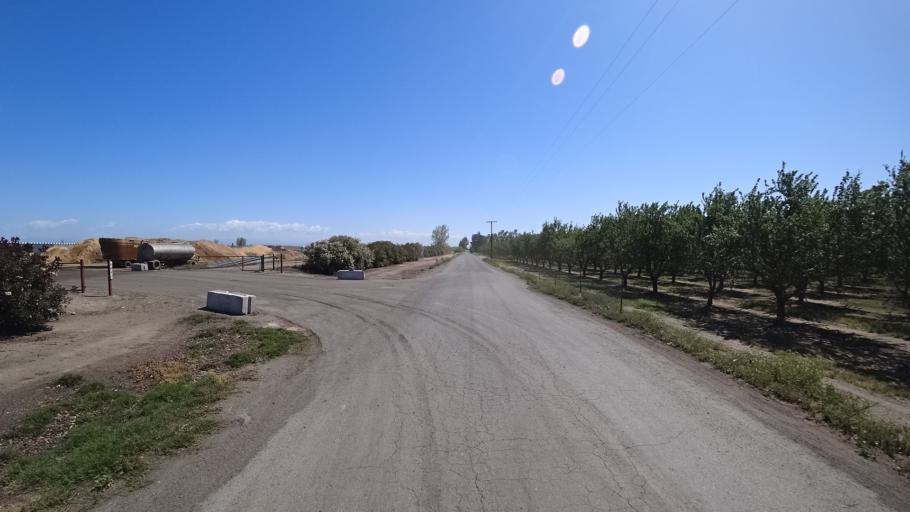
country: US
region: California
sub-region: Glenn County
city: Orland
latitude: 39.6819
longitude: -122.1583
